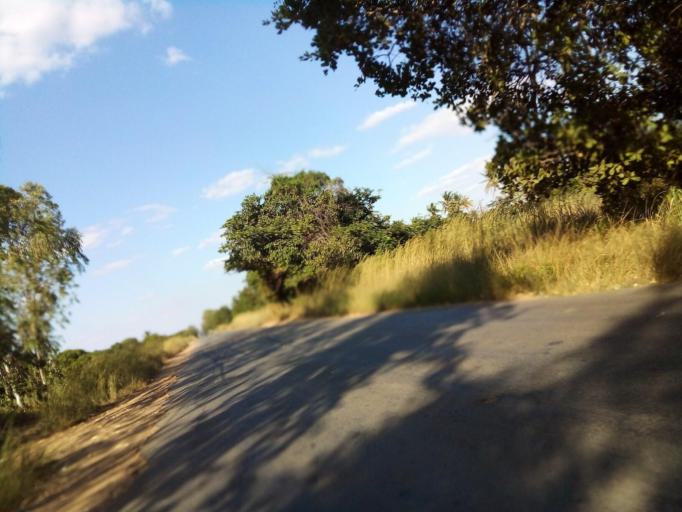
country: MZ
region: Zambezia
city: Quelimane
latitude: -17.5758
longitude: 36.6349
